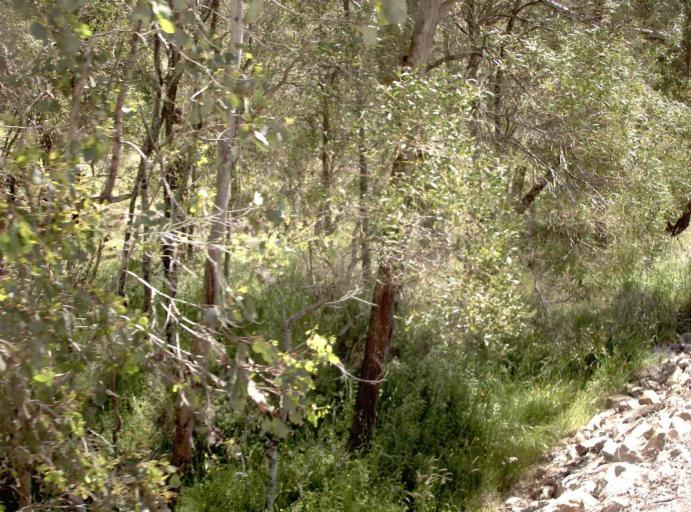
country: AU
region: Victoria
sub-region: East Gippsland
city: Lakes Entrance
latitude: -37.2313
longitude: 148.2611
